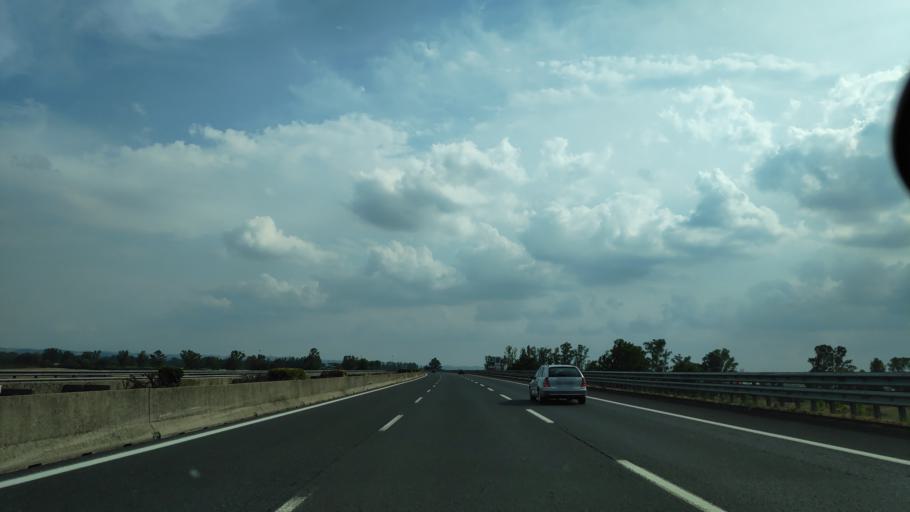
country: IT
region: Latium
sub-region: Citta metropolitana di Roma Capitale
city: Bivio di Capanelle
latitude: 42.1353
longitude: 12.6185
